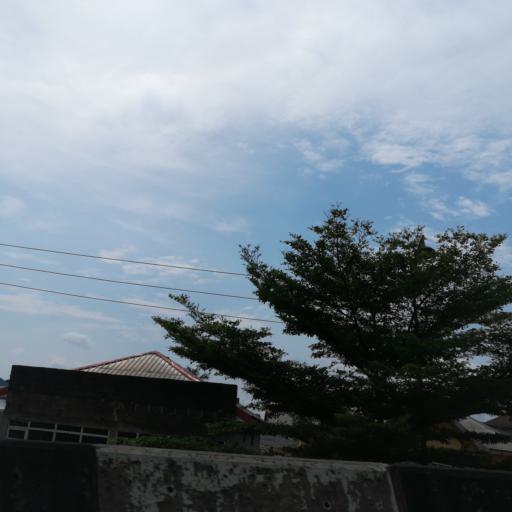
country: NG
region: Rivers
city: Port Harcourt
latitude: 4.8581
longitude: 7.0222
